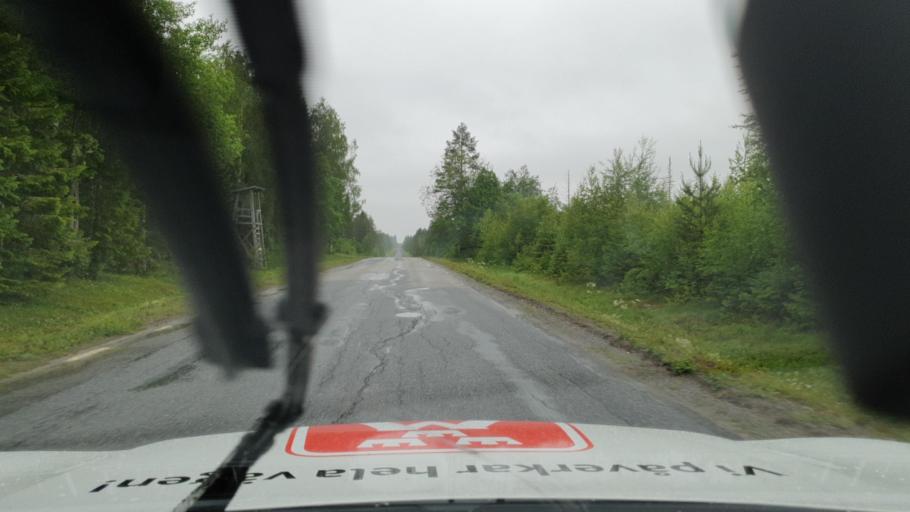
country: SE
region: Vaesterbotten
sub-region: Nordmalings Kommun
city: Nordmaling
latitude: 63.8190
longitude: 19.4951
